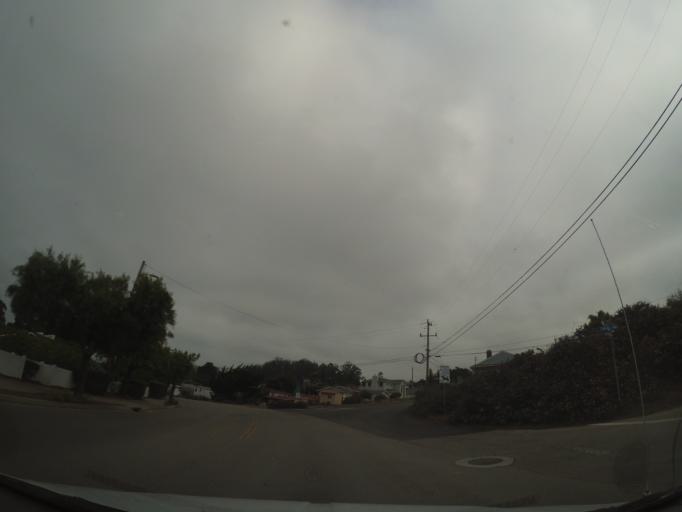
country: US
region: California
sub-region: San Luis Obispo County
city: Morro Bay
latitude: 35.3556
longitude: -120.8444
